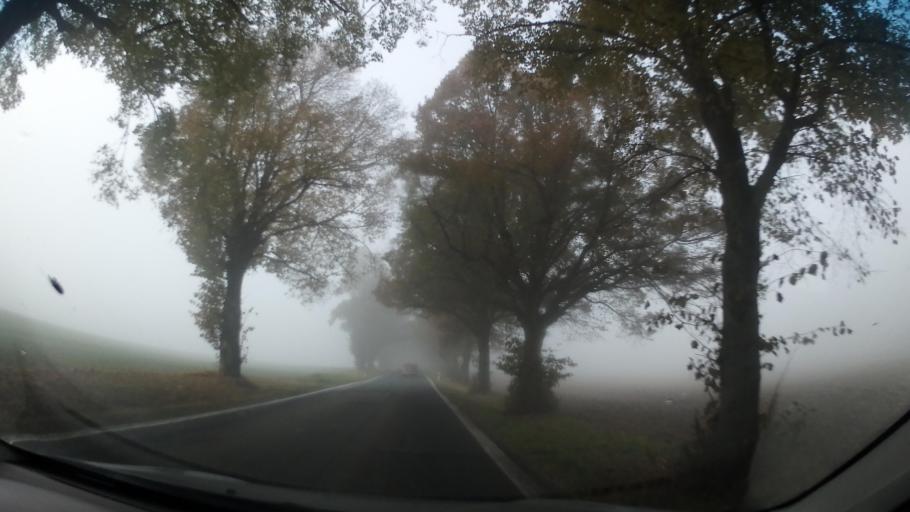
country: CZ
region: Vysocina
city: Krizanov
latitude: 49.4694
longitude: 16.0992
